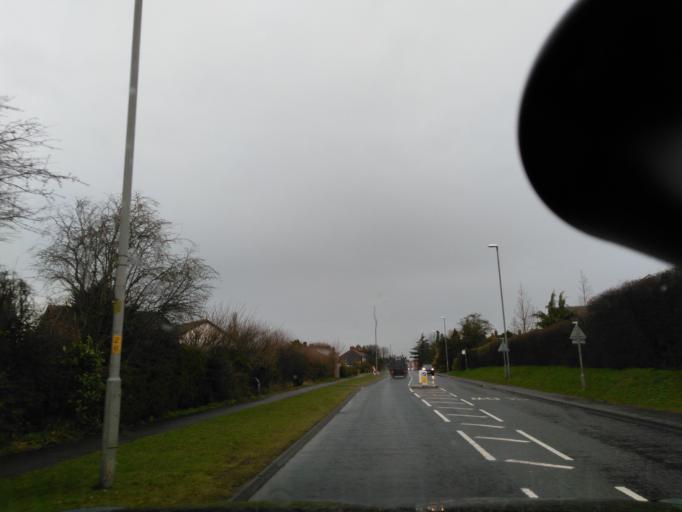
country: GB
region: England
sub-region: North Yorkshire
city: Northallerton
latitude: 54.3292
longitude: -1.4278
